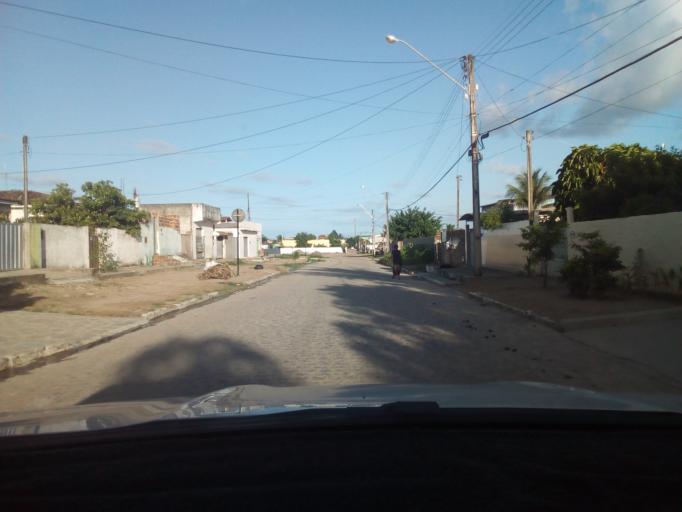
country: BR
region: Paraiba
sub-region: Joao Pessoa
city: Joao Pessoa
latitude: -7.1789
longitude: -34.8209
